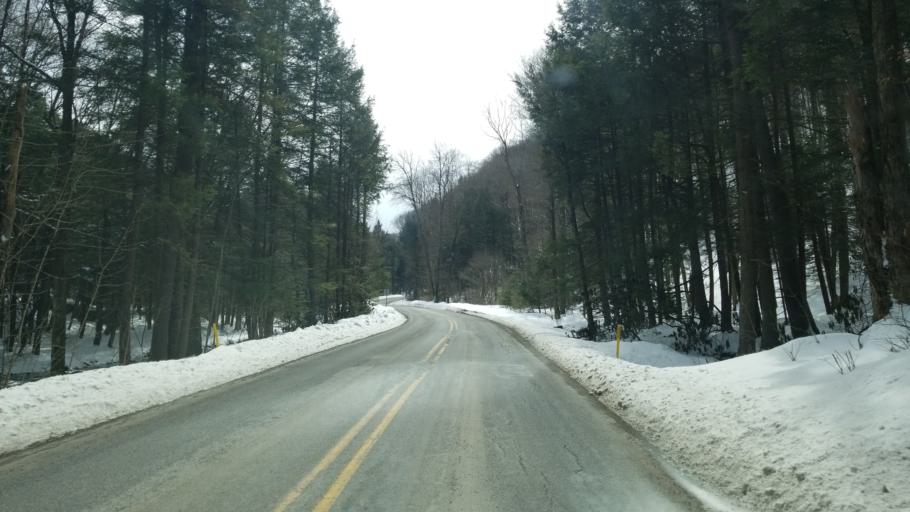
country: US
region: Pennsylvania
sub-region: Clearfield County
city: Shiloh
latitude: 41.2569
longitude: -78.1520
